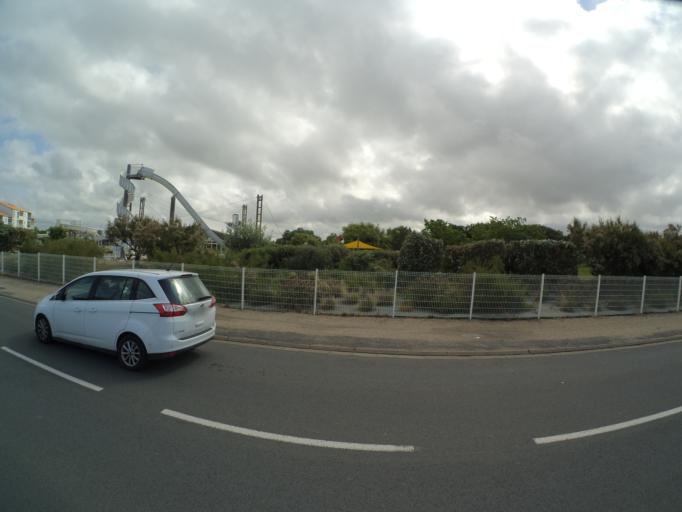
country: FR
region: Poitou-Charentes
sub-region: Departement de la Charente-Maritime
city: Chatelaillon-Plage
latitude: 46.0621
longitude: -1.0915
